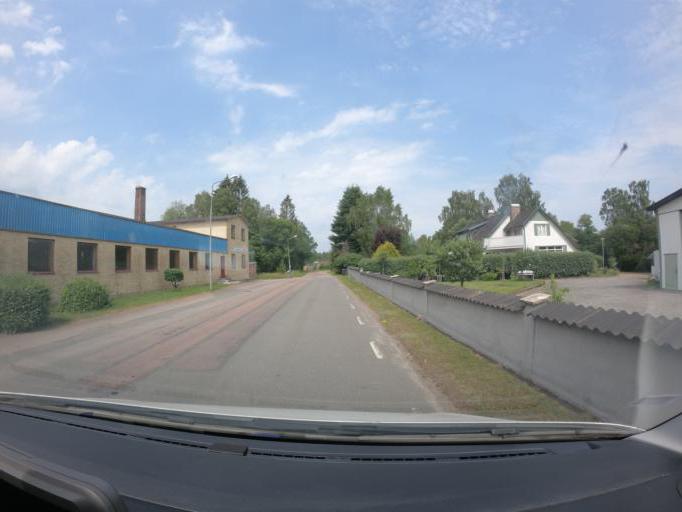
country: SE
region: Skane
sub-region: Hassleholms Kommun
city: Bjarnum
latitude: 56.2419
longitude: 13.7082
